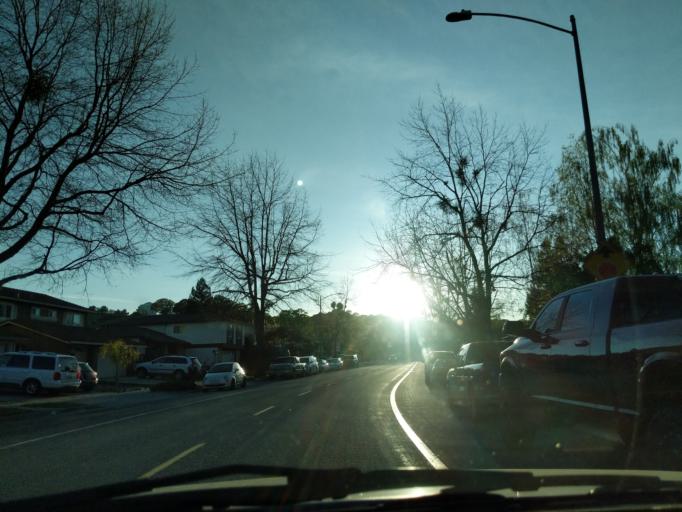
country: US
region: California
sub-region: Santa Clara County
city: Gilroy
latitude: 37.0282
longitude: -121.6073
